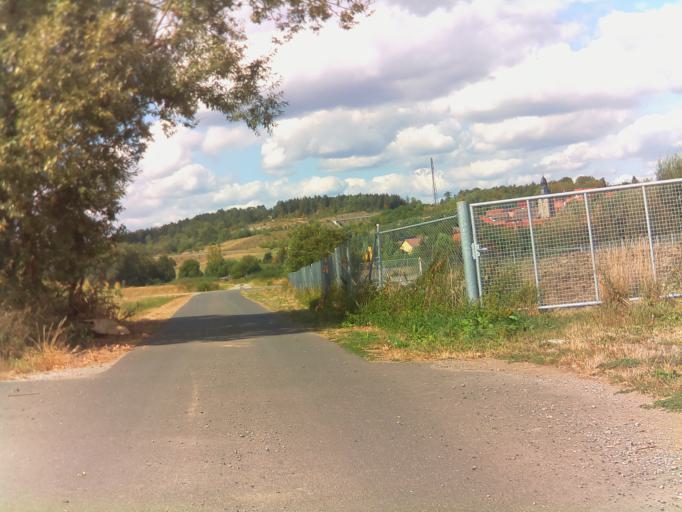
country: DE
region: Thuringia
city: Wolfershausen
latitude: 50.4445
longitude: 10.4554
